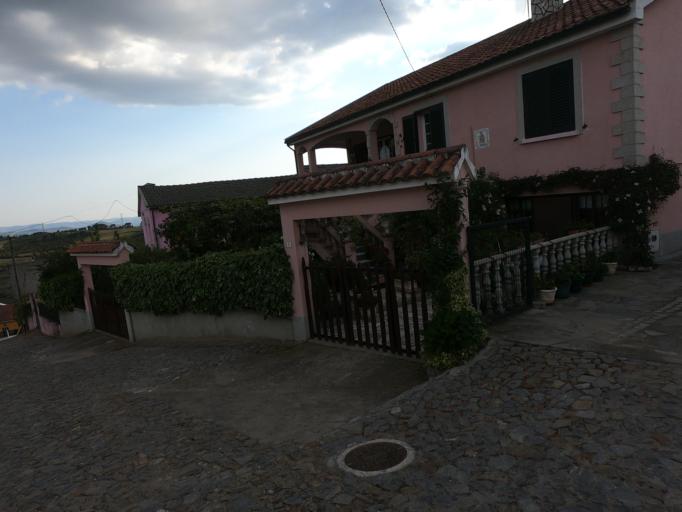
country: PT
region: Vila Real
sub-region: Sabrosa
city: Vilela
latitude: 41.2120
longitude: -7.6641
